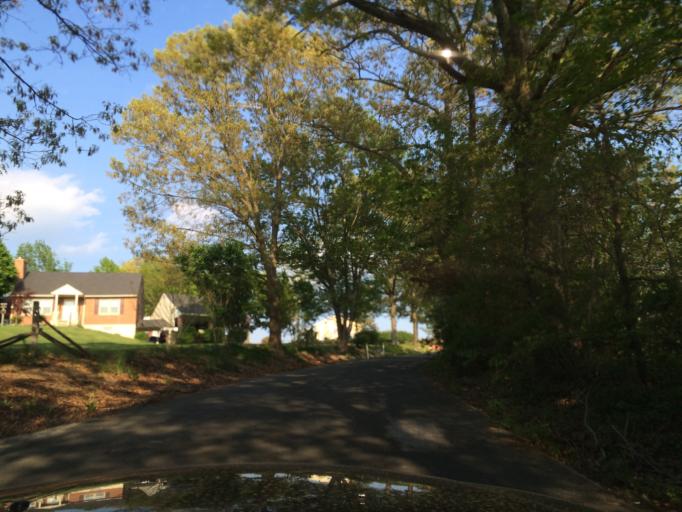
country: US
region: Maryland
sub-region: Carroll County
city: New Windsor
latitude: 39.4855
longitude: -77.0365
